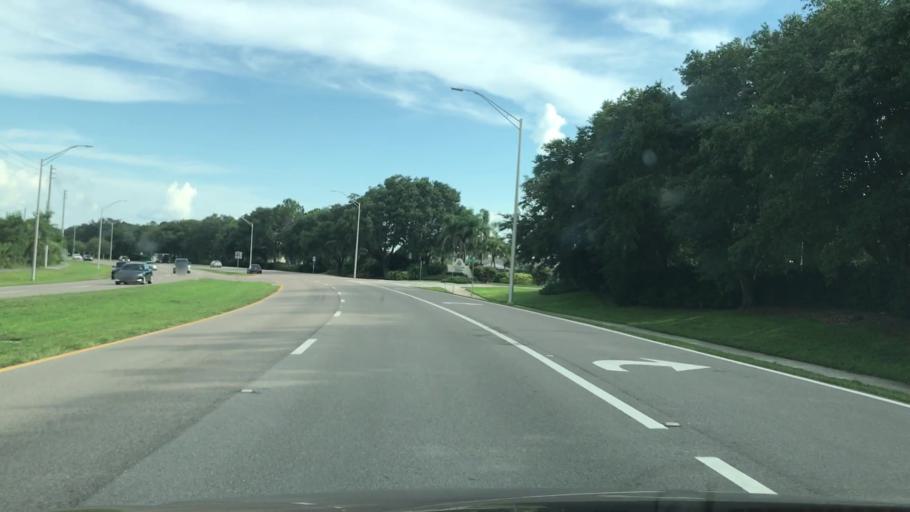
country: US
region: Florida
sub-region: Sarasota County
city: Venice Gardens
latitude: 27.0911
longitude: -82.3892
